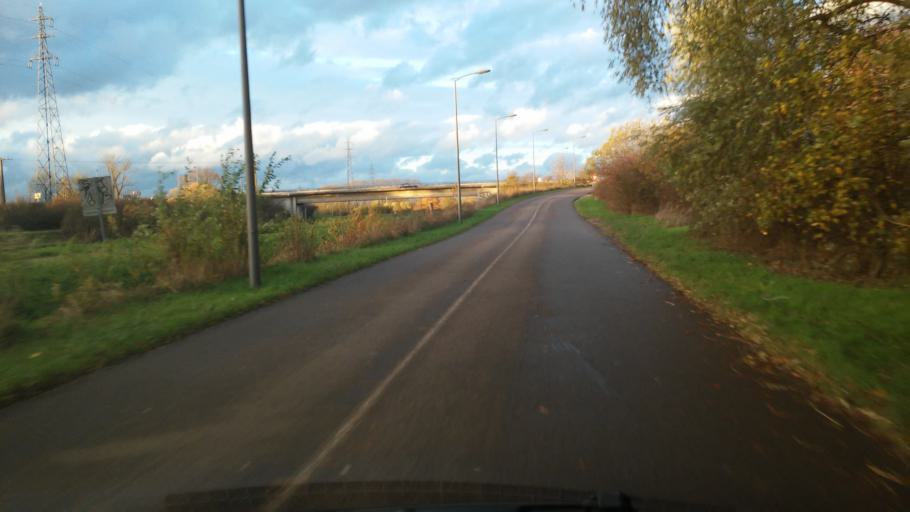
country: FR
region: Lorraine
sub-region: Departement de la Moselle
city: Talange
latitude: 49.2402
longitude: 6.1829
